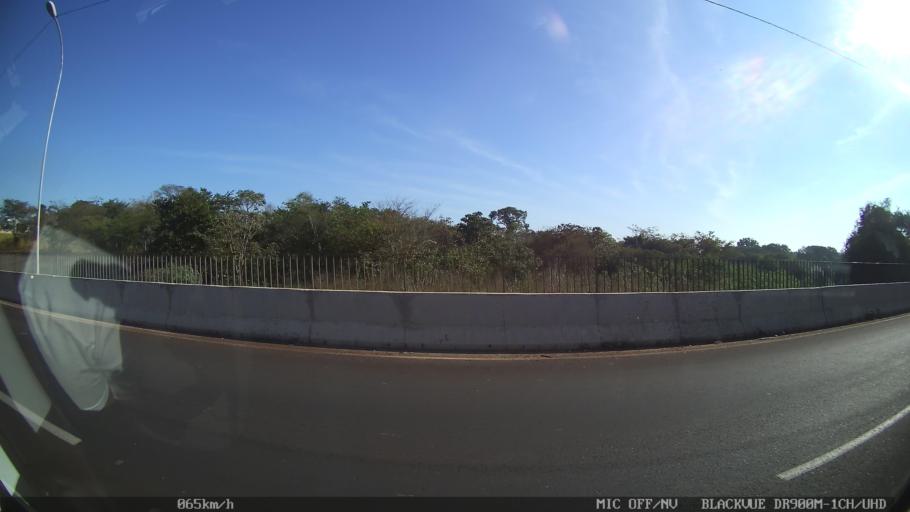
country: BR
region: Sao Paulo
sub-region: Sao Jose Do Rio Preto
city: Sao Jose do Rio Preto
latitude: -20.7622
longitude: -49.3750
